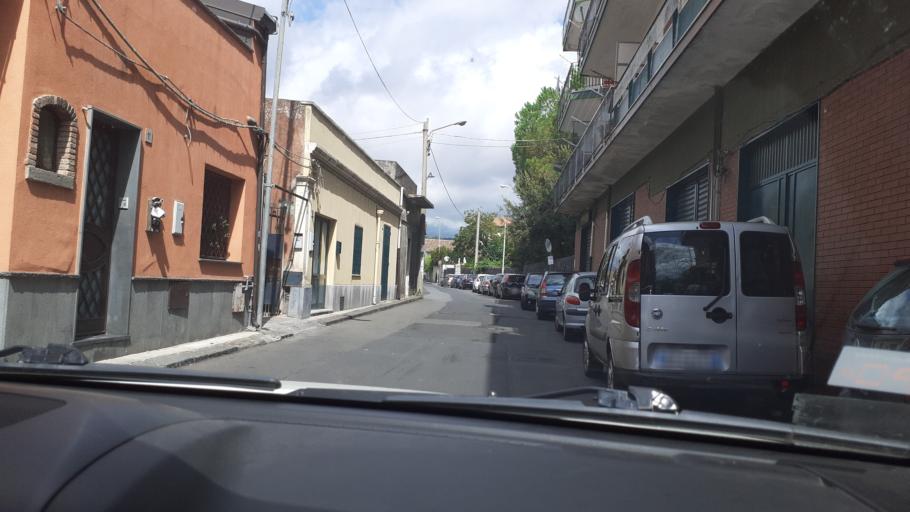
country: IT
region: Sicily
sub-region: Catania
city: San Giovanni la Punta
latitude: 37.5847
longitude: 15.0963
